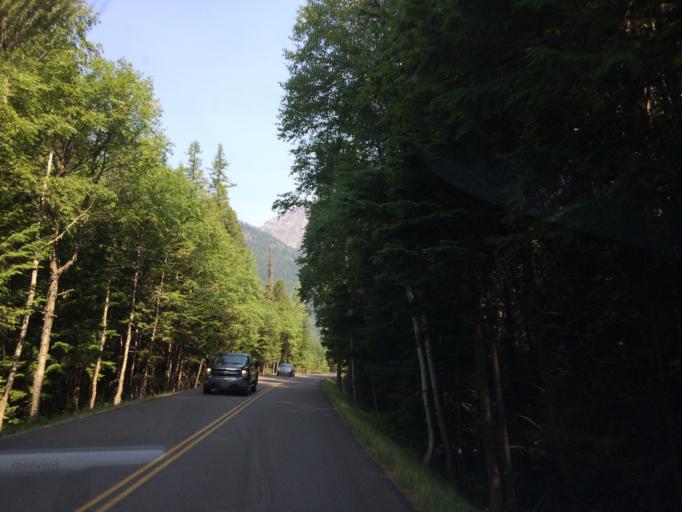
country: US
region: Montana
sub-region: Flathead County
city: Columbia Falls
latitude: 48.6370
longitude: -113.8640
